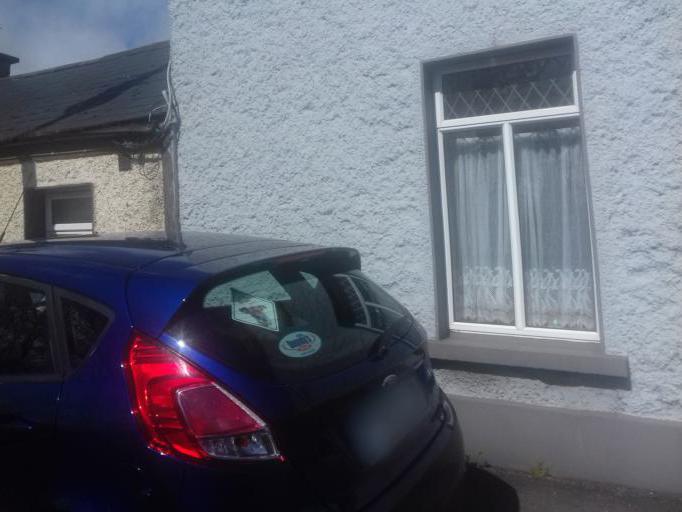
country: IE
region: Leinster
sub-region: Laois
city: Portlaoise
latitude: 53.0366
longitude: -7.2960
